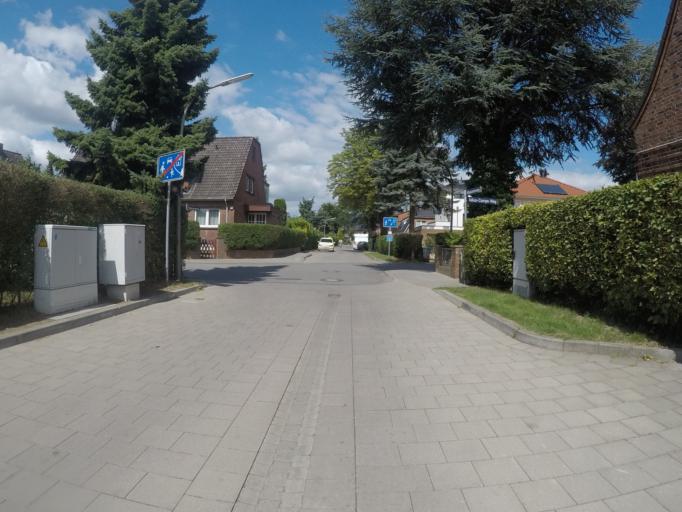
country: DE
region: Hamburg
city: Wandsbek
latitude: 53.5453
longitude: 10.1097
